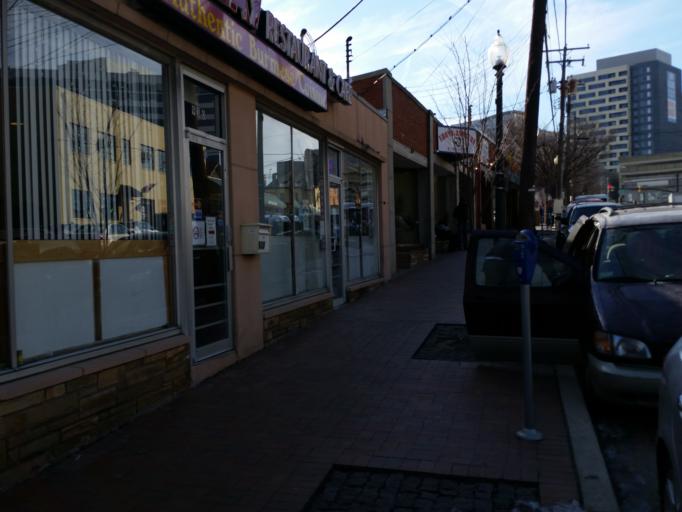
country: US
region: Maryland
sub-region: Montgomery County
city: Silver Spring
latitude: 38.9939
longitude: -77.0252
